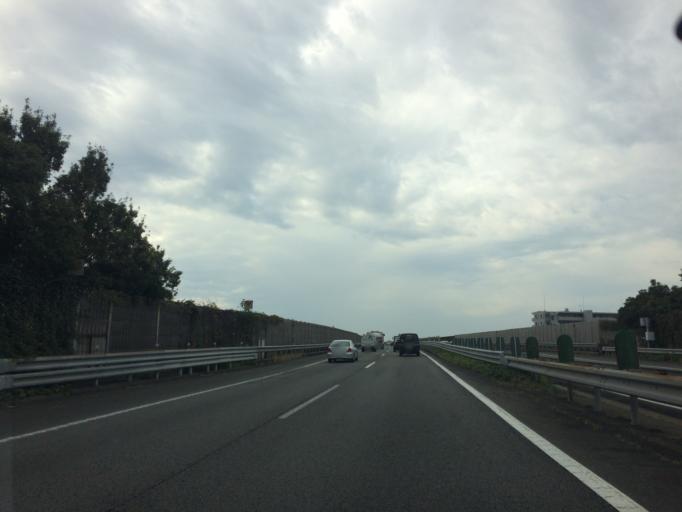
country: JP
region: Shizuoka
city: Fujieda
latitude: 34.8608
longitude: 138.2833
